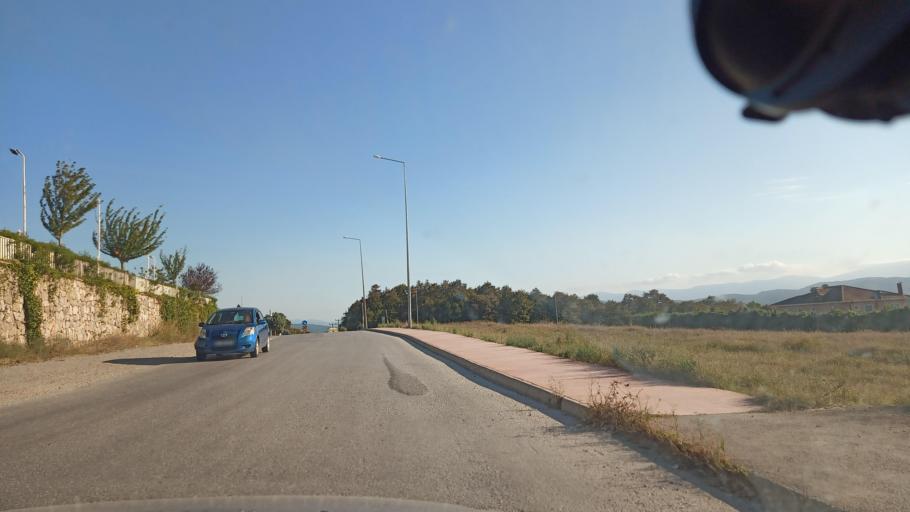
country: TR
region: Sakarya
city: Kazimpasa
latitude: 40.8510
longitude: 30.2790
